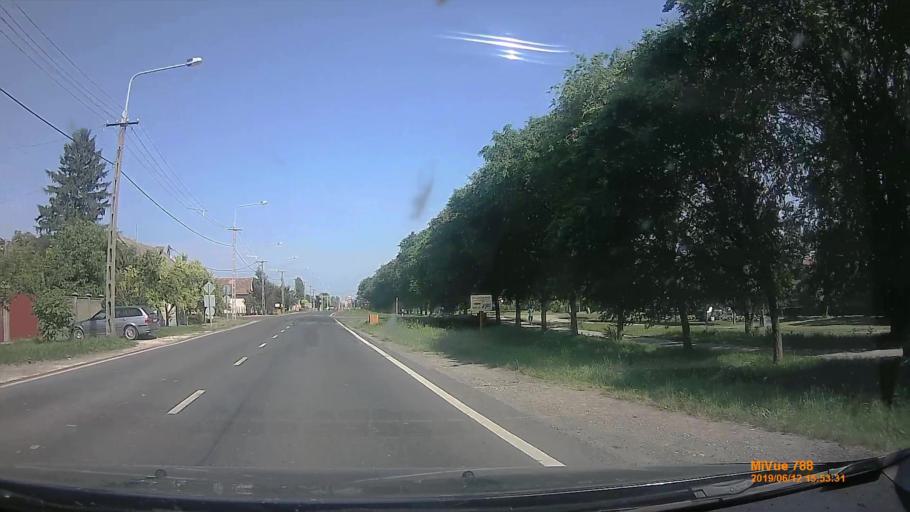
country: HU
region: Csongrad
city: Apatfalva
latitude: 46.1730
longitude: 20.5855
